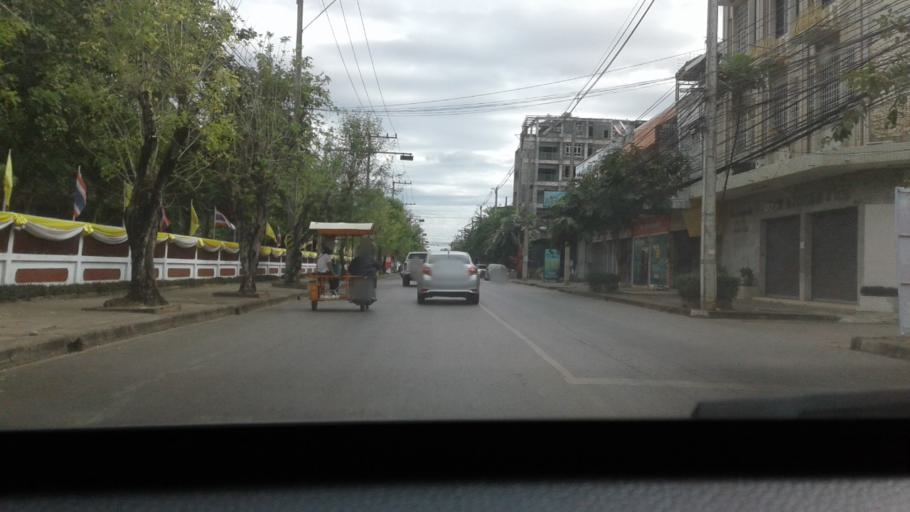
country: TH
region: Changwat Udon Thani
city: Udon Thani
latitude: 17.4127
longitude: 102.7934
